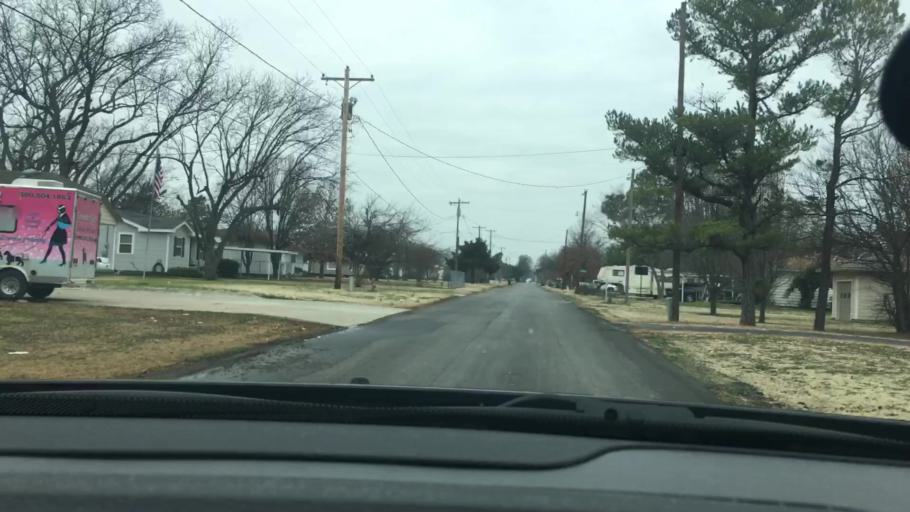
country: US
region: Oklahoma
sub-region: Carter County
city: Healdton
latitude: 34.2164
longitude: -97.4687
